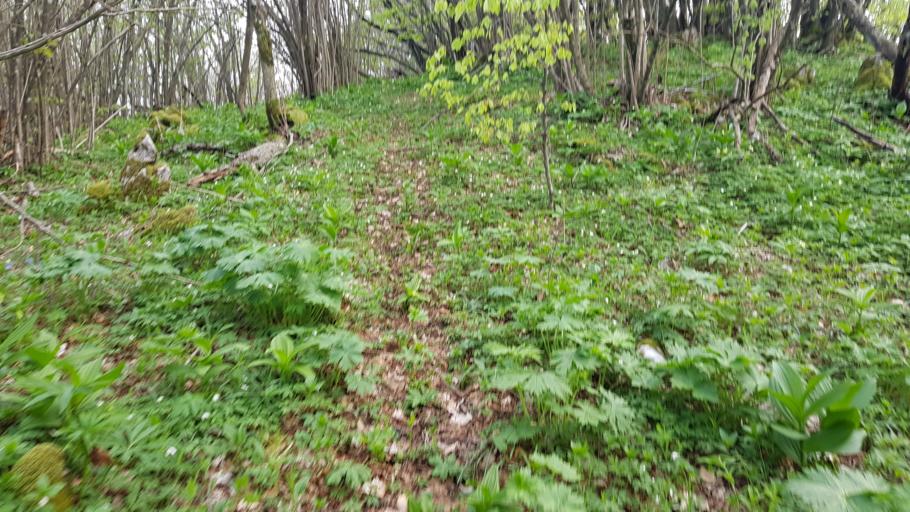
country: IT
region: Friuli Venezia Giulia
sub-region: Provincia di Udine
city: Taipana
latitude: 46.2220
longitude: 13.3589
